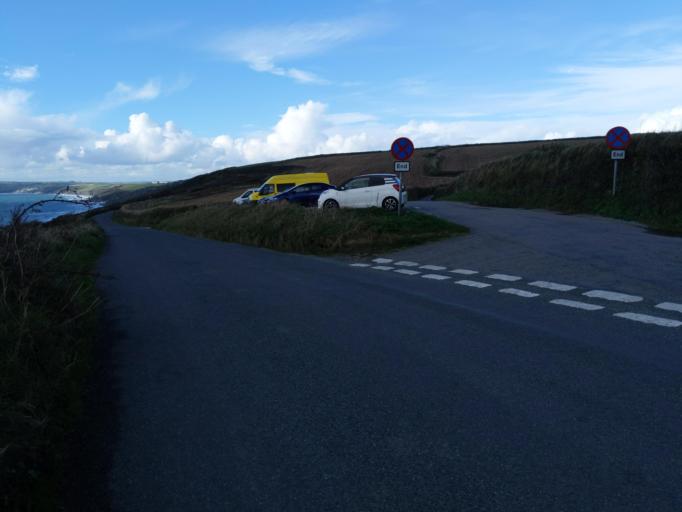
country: GB
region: England
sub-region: Cornwall
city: Torpoint
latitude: 50.3312
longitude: -4.2219
